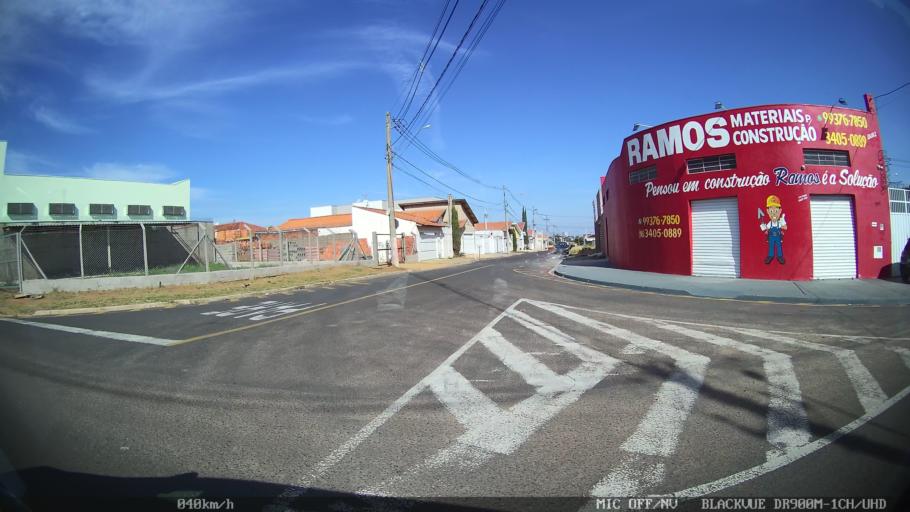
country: BR
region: Sao Paulo
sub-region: Franca
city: Franca
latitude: -20.5085
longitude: -47.4254
